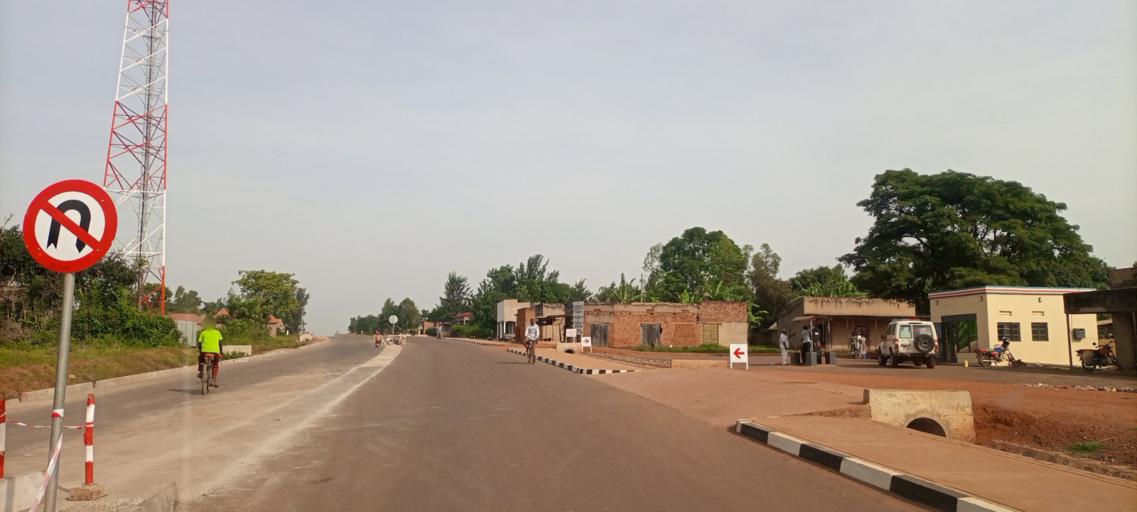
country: UG
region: Eastern Region
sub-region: Budaka District
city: Budaka
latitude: 1.1007
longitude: 34.0111
